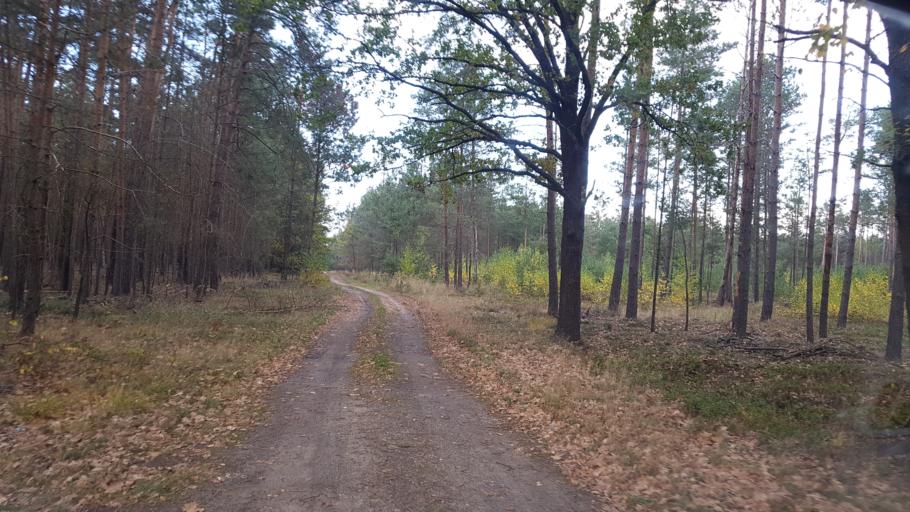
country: DE
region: Brandenburg
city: Schonborn
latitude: 51.6485
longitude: 13.5086
